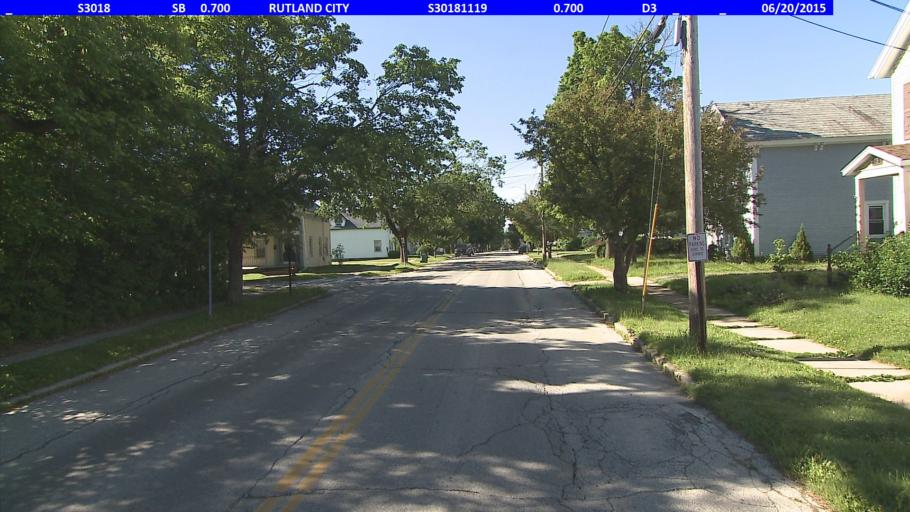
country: US
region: Vermont
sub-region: Rutland County
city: Rutland
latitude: 43.6028
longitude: -72.9839
